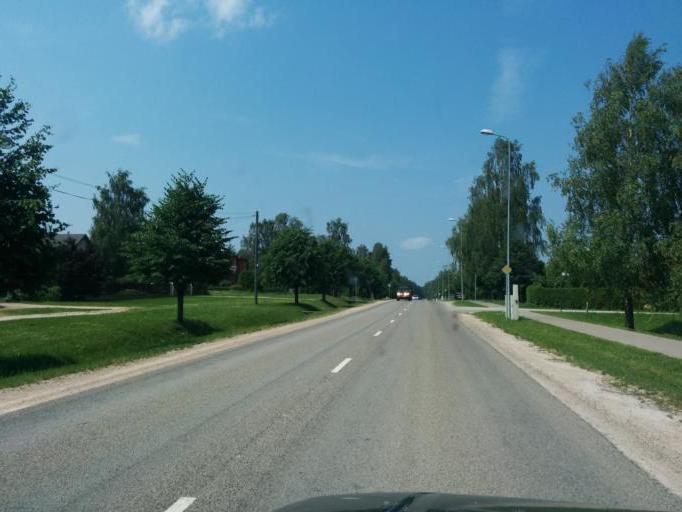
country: LV
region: Baldone
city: Baldone
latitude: 56.7432
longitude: 24.3818
